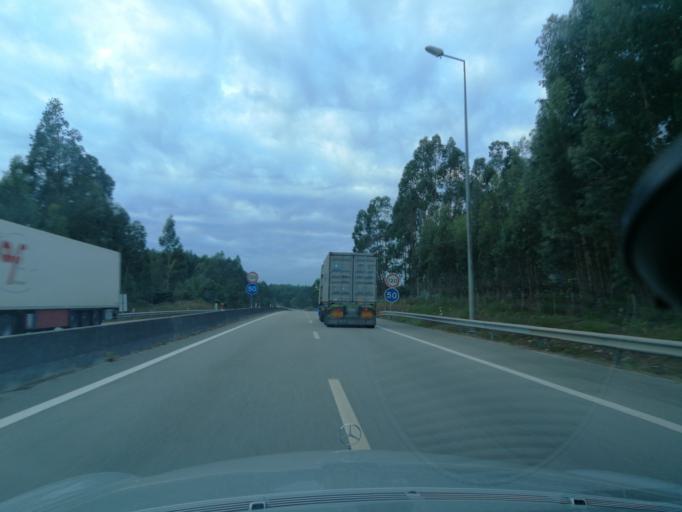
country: PT
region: Aveiro
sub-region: Albergaria-A-Velha
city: Albergaria-a-Velha
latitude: 40.6763
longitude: -8.4777
